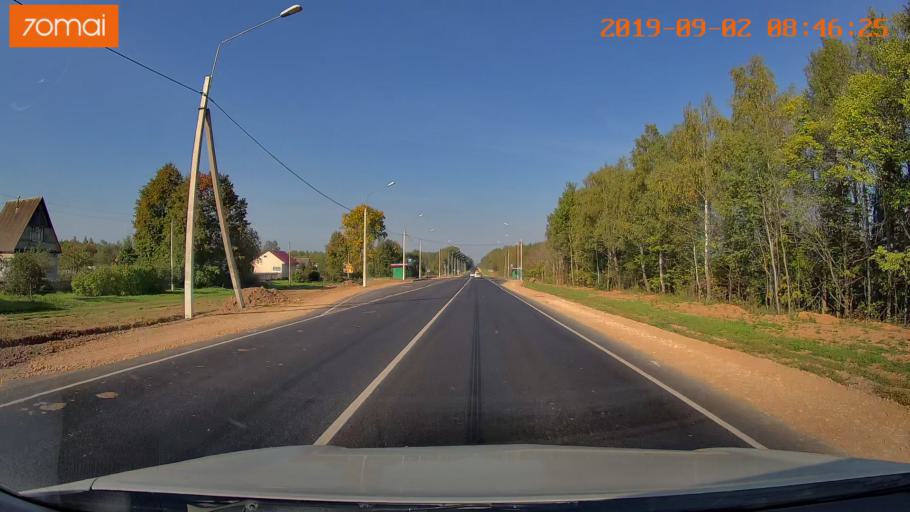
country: RU
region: Kaluga
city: Medyn'
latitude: 54.9687
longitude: 35.9787
